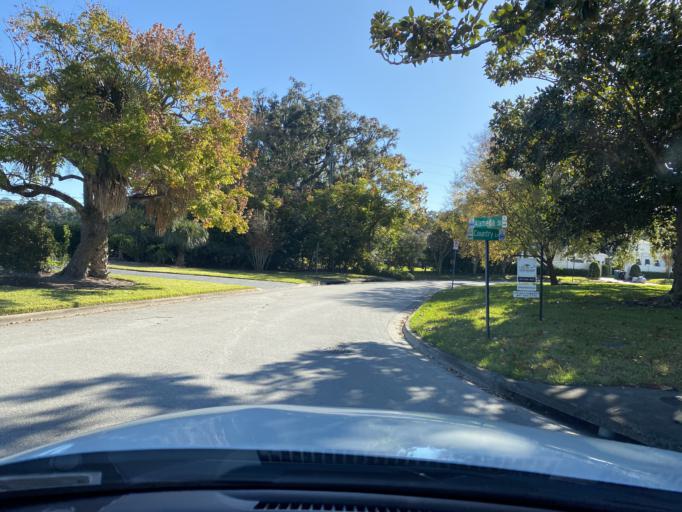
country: US
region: Florida
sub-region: Orange County
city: Orlando
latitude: 28.5570
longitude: -81.4062
